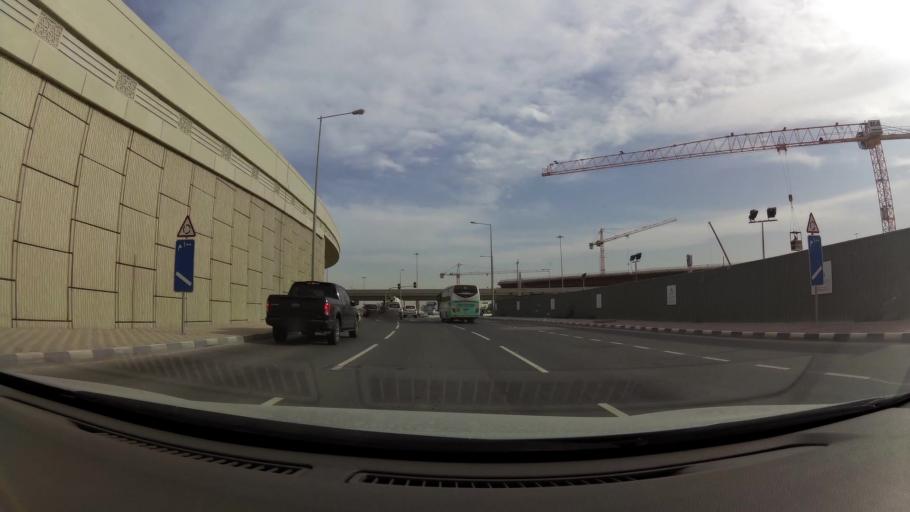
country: QA
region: Baladiyat ar Rayyan
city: Ar Rayyan
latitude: 25.2969
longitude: 51.4743
